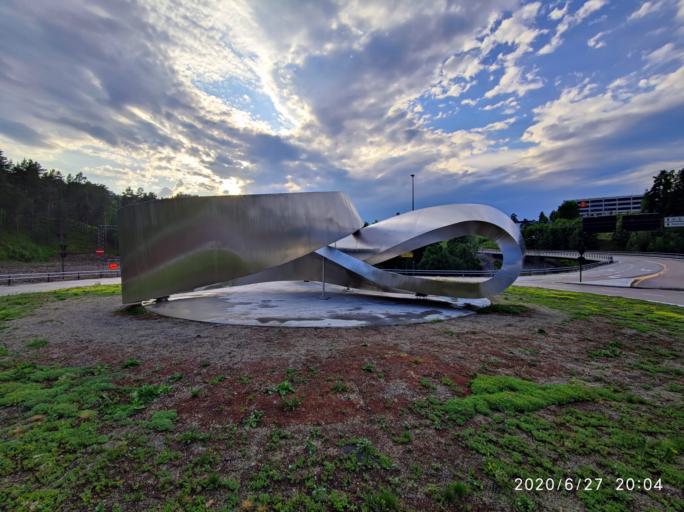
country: NO
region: Buskerud
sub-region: Kongsberg
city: Kongsberg
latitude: 59.6487
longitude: 9.6475
